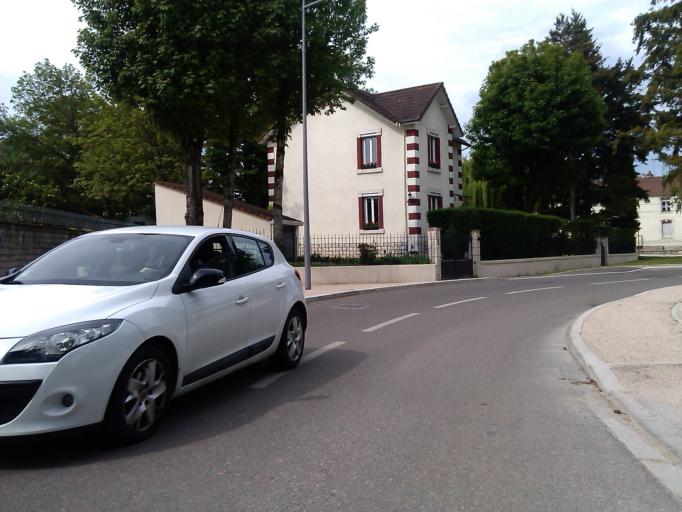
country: FR
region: Franche-Comte
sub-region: Departement du Jura
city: Dole
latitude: 47.1023
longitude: 5.4995
